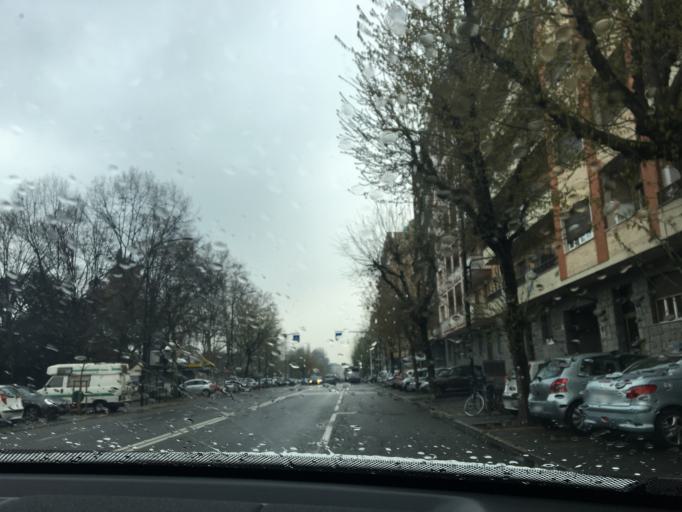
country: IT
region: Piedmont
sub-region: Provincia di Torino
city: Moncalieri
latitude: 45.0238
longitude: 7.6679
